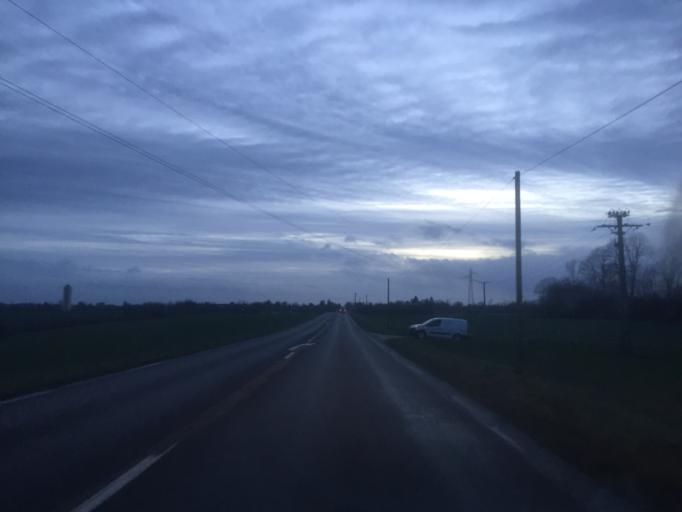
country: FR
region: Franche-Comte
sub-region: Departement du Jura
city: Dole
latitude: 47.1092
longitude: 5.5247
